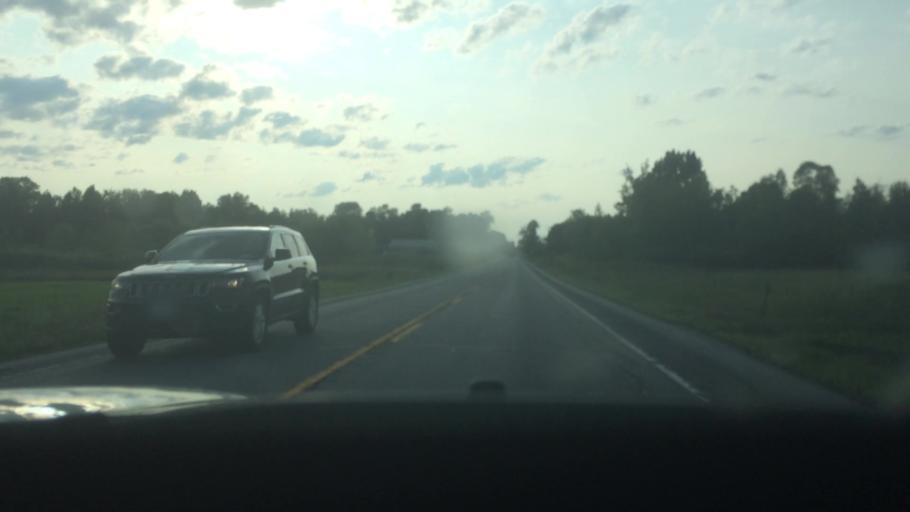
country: US
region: New York
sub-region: St. Lawrence County
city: Ogdensburg
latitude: 44.6728
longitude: -75.3933
